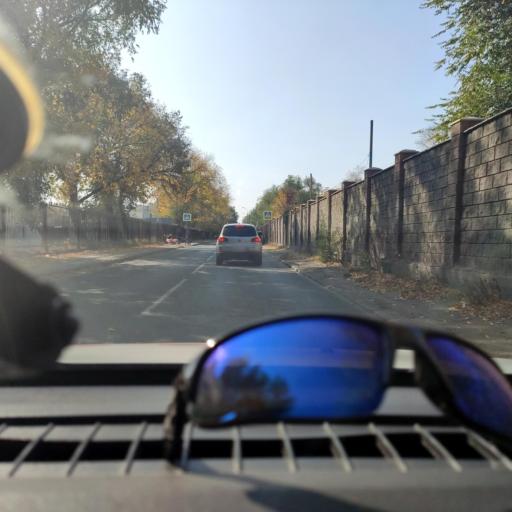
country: RU
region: Samara
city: Petra-Dubrava
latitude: 53.2395
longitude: 50.2710
